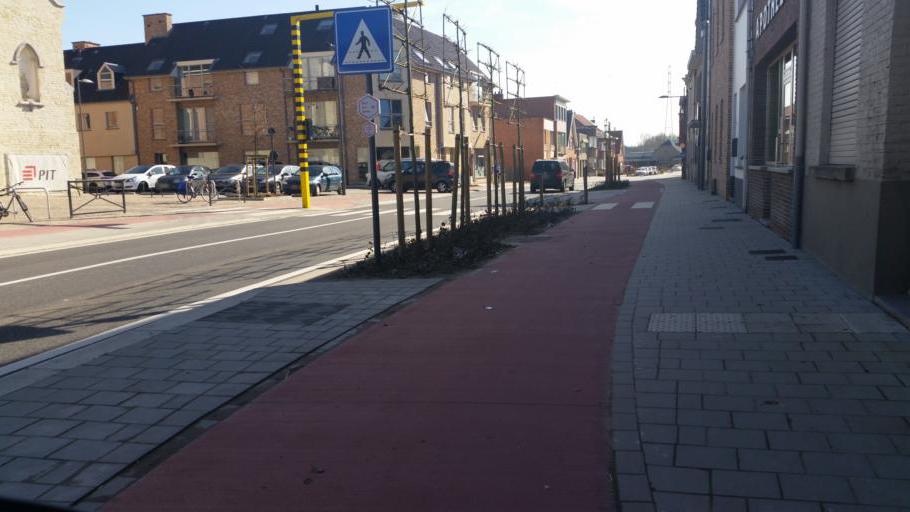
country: BE
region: Flanders
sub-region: Provincie Vlaams-Brabant
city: Zemst
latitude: 50.9601
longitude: 4.4971
